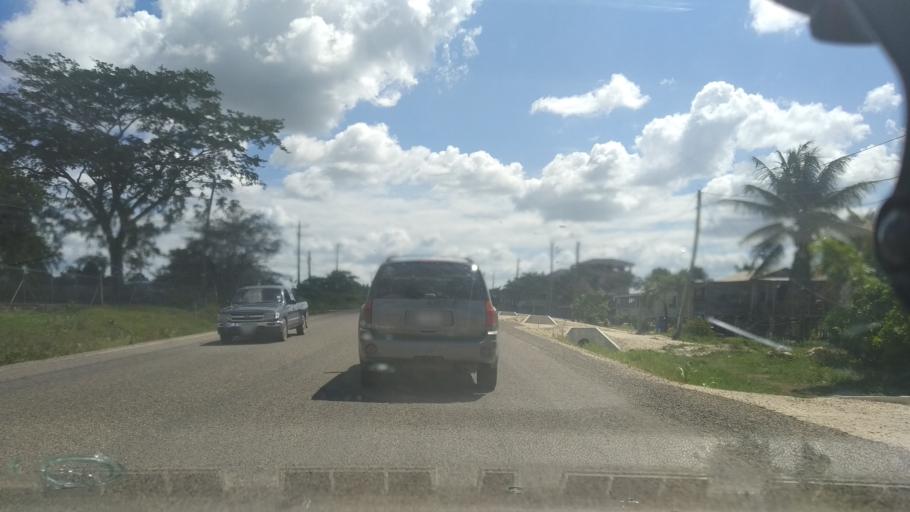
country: BZ
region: Cayo
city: Belmopan
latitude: 17.2555
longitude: -88.8089
